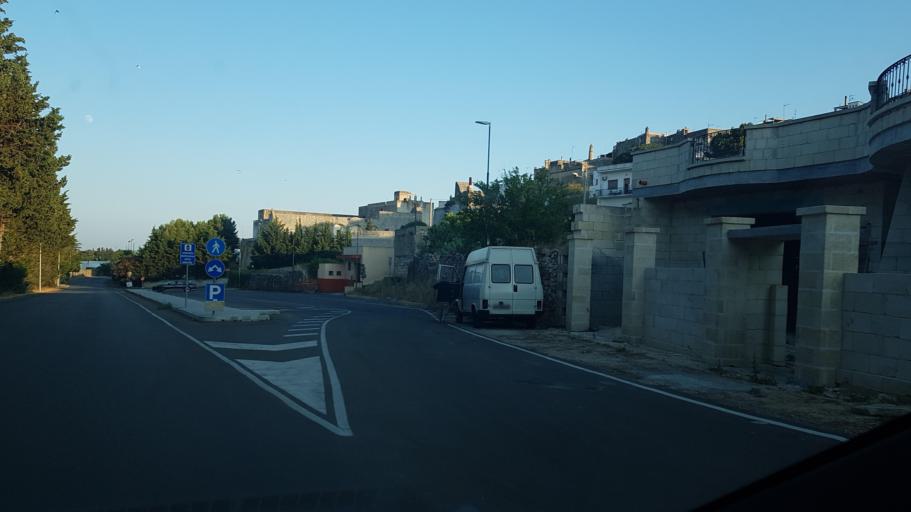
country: IT
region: Apulia
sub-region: Provincia di Lecce
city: Specchia
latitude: 39.9443
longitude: 18.2995
